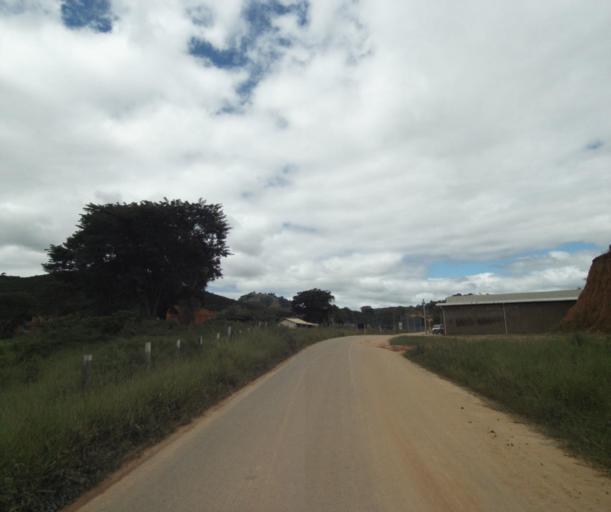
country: BR
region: Espirito Santo
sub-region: Irupi
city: Irupi
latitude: -20.3380
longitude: -41.6450
